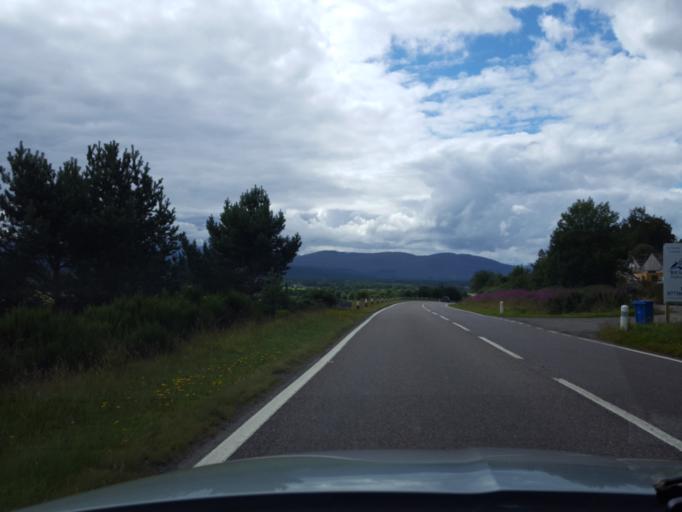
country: GB
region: Scotland
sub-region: Highland
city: Grantown on Spey
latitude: 57.2850
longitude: -3.6685
